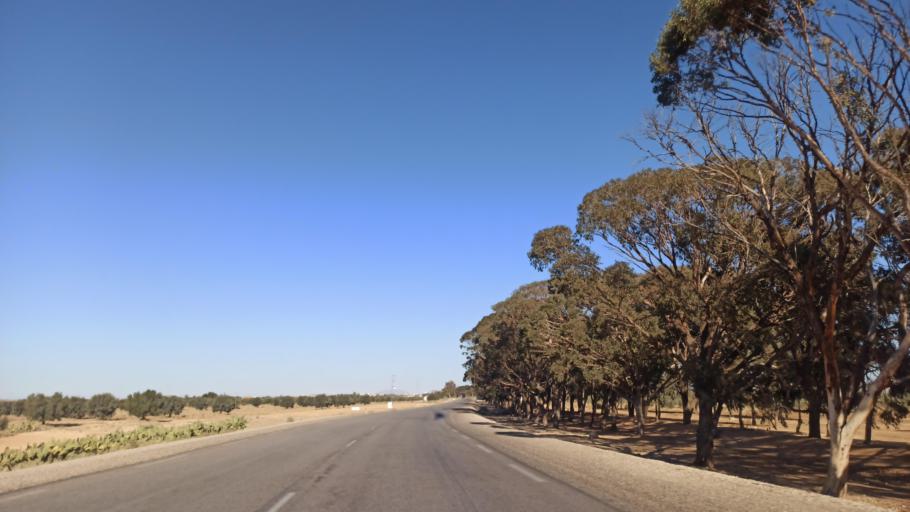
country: TN
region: Sidi Bu Zayd
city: Jilma
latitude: 35.2411
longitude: 9.3908
